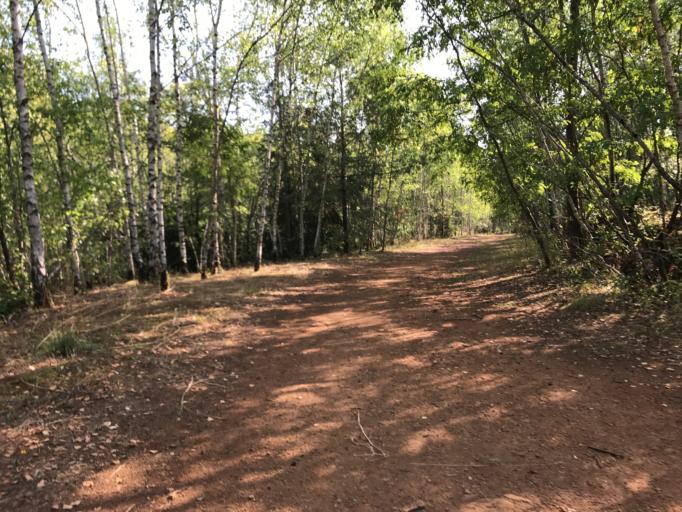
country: LU
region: Luxembourg
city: Lamadelaine
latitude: 49.5414
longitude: 5.8722
